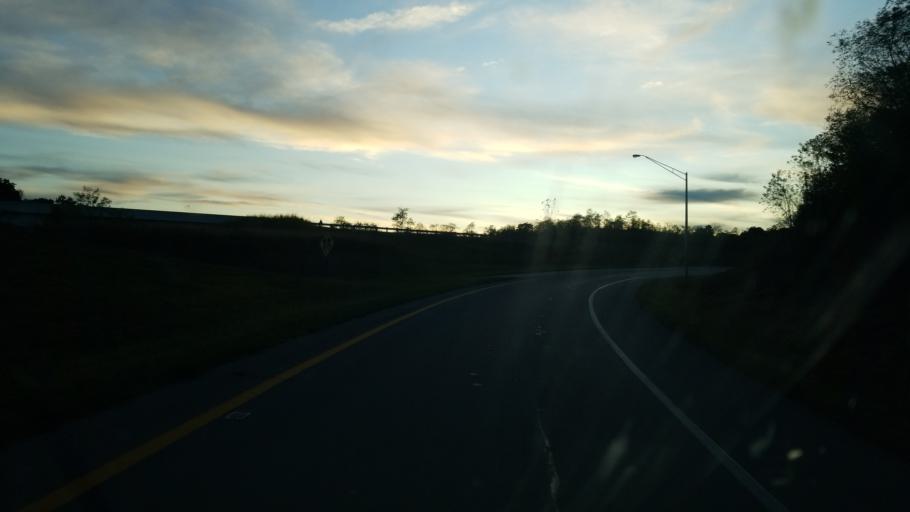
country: US
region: Ohio
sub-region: Meigs County
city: Pomeroy
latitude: 39.0538
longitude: -81.9730
